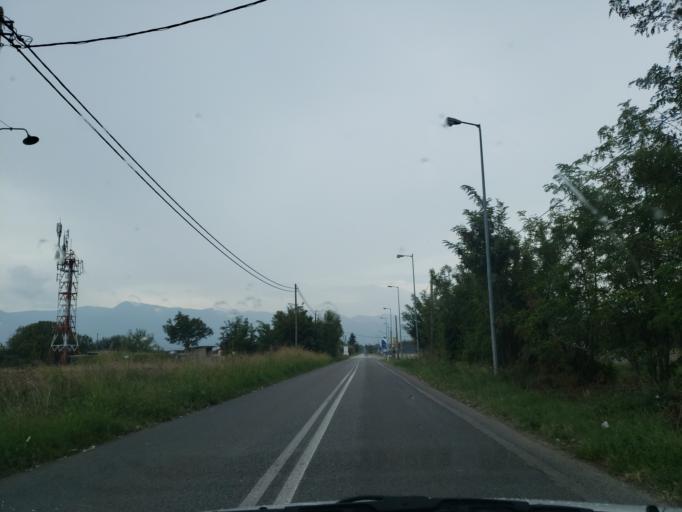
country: GR
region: Central Greece
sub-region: Nomos Fthiotidos
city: Rodhitsa
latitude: 38.8623
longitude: 22.4400
